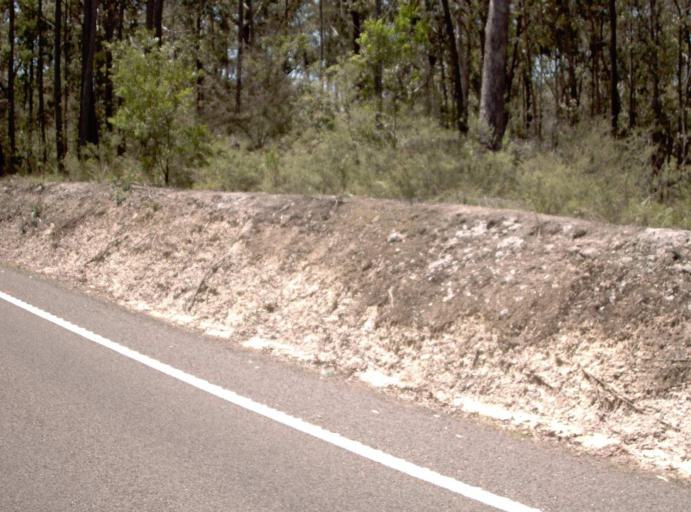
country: AU
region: Victoria
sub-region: East Gippsland
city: Lakes Entrance
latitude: -37.7622
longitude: 148.0597
